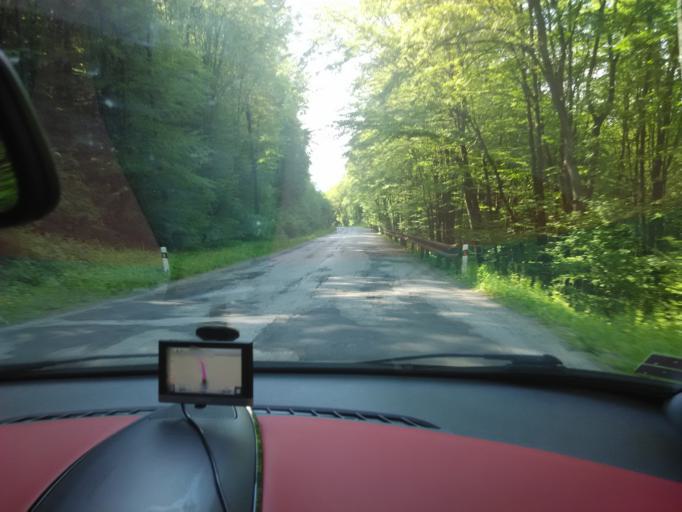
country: SK
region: Banskobystricky
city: Revuca
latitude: 48.6263
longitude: 20.2714
